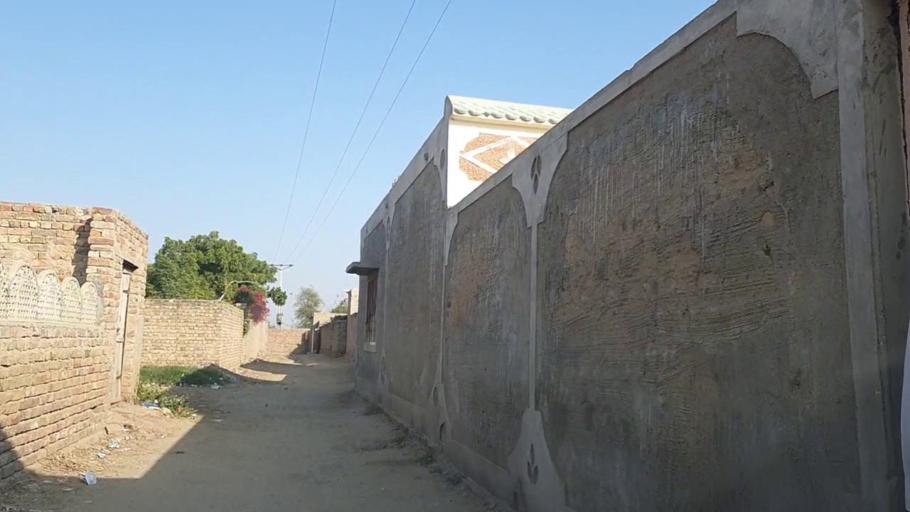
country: PK
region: Sindh
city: Naukot
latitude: 24.9021
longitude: 69.4626
